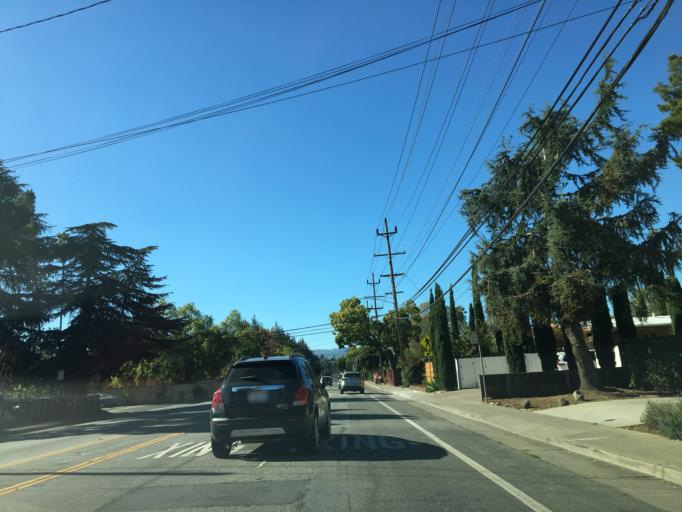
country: US
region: California
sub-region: Santa Clara County
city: Los Altos
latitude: 37.4138
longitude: -122.1197
